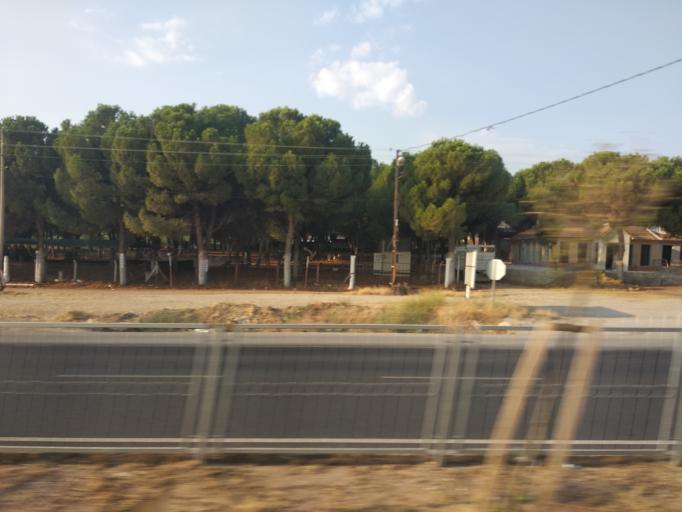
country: TR
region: Manisa
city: Ahmetli
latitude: 38.5050
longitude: 28.0042
